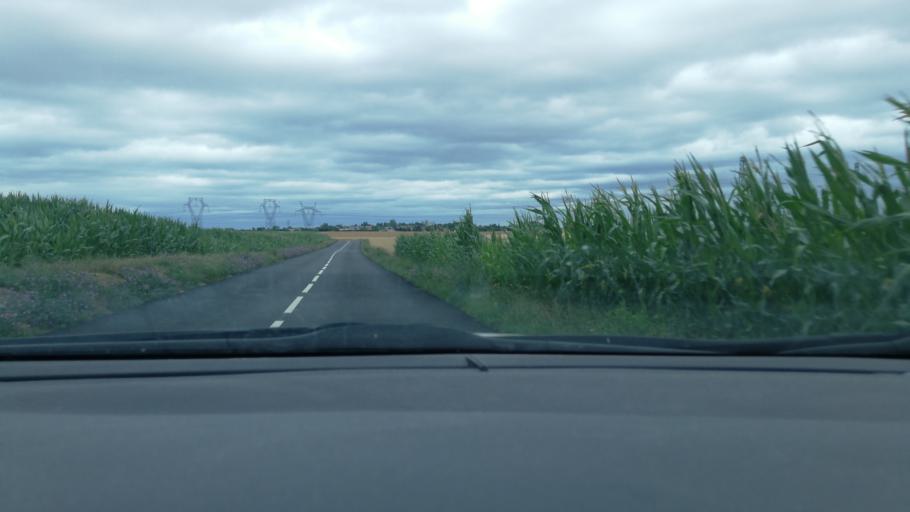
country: FR
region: Ile-de-France
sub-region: Departement du Val-d'Oise
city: Ennery
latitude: 49.0987
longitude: 2.1043
